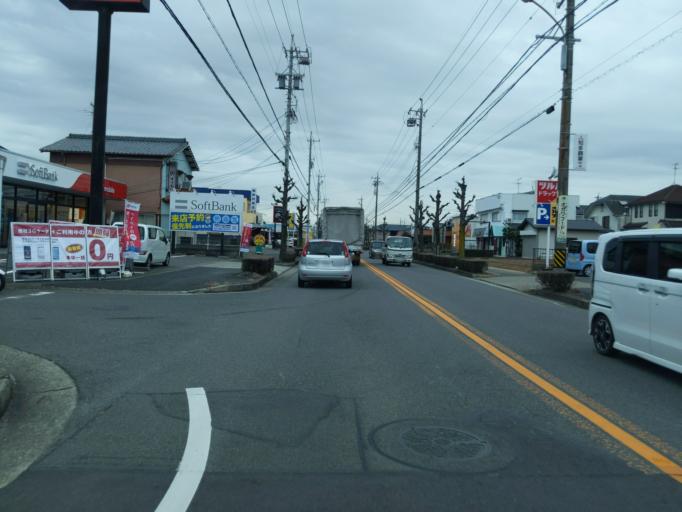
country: JP
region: Aichi
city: Kasugai
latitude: 35.2588
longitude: 136.9534
